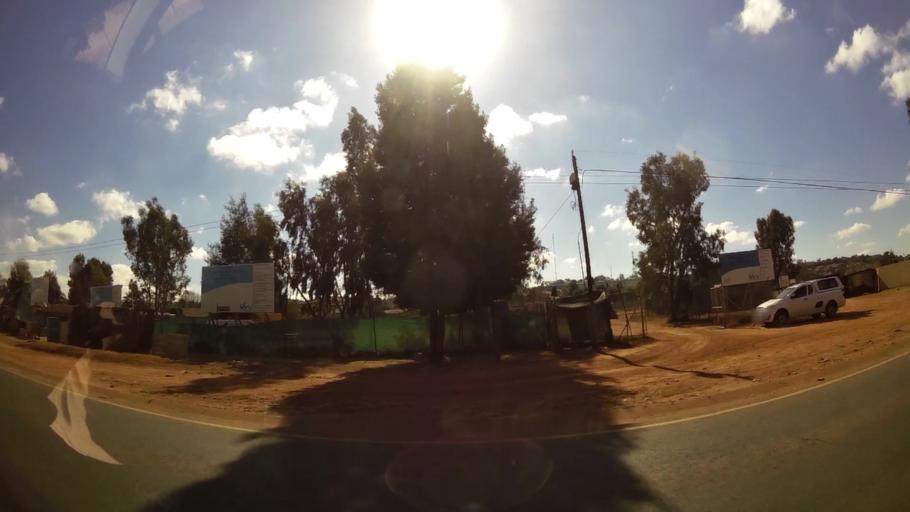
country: ZA
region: Gauteng
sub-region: City of Johannesburg Metropolitan Municipality
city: Roodepoort
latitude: -26.1080
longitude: 27.8530
